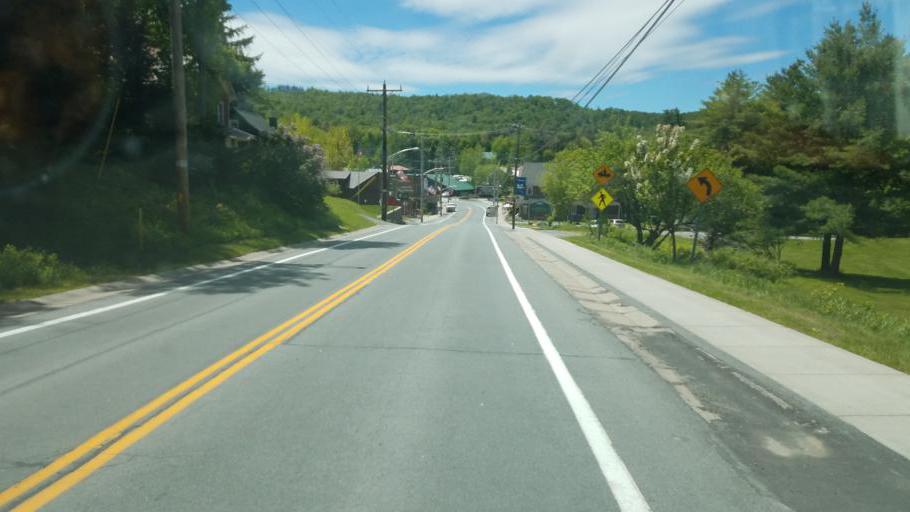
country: US
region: New York
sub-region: Hamilton County
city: Lake Pleasant
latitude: 43.7534
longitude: -74.7934
